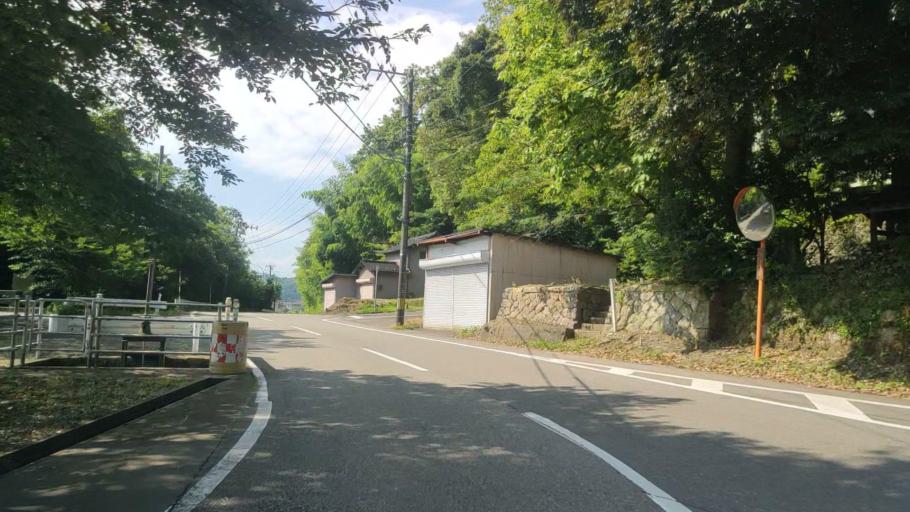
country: JP
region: Ishikawa
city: Komatsu
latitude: 36.3782
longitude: 136.4965
